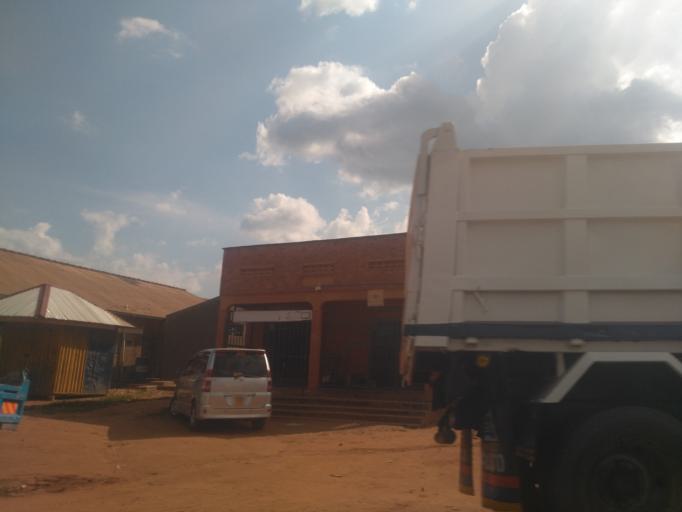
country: UG
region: Central Region
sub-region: Wakiso District
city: Kajansi
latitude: 0.2781
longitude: 32.4761
